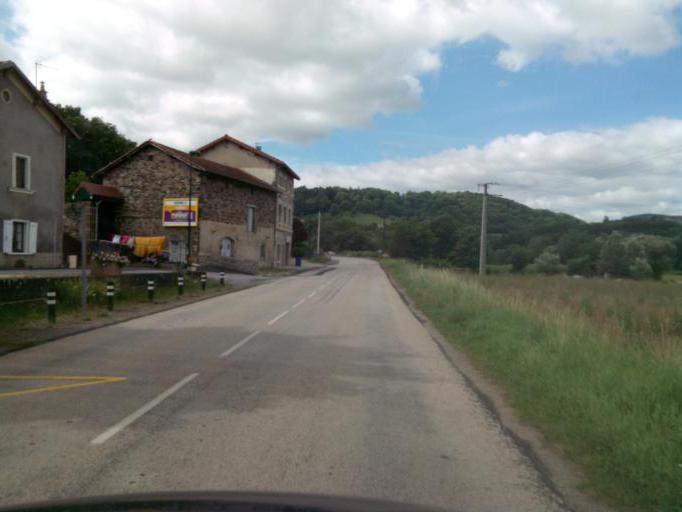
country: FR
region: Auvergne
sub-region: Departement de la Haute-Loire
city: Chadrac
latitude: 45.0735
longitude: 3.9041
